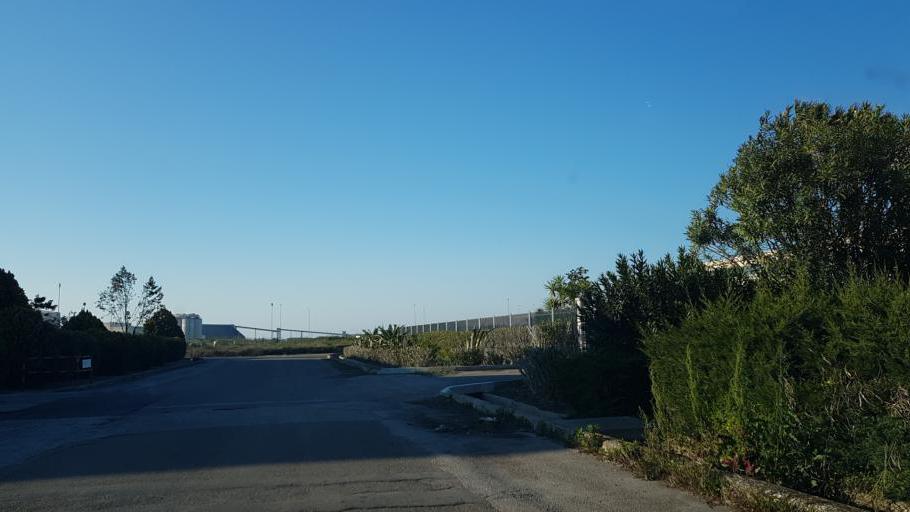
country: IT
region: Apulia
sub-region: Provincia di Brindisi
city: Materdomini
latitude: 40.6301
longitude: 17.9677
